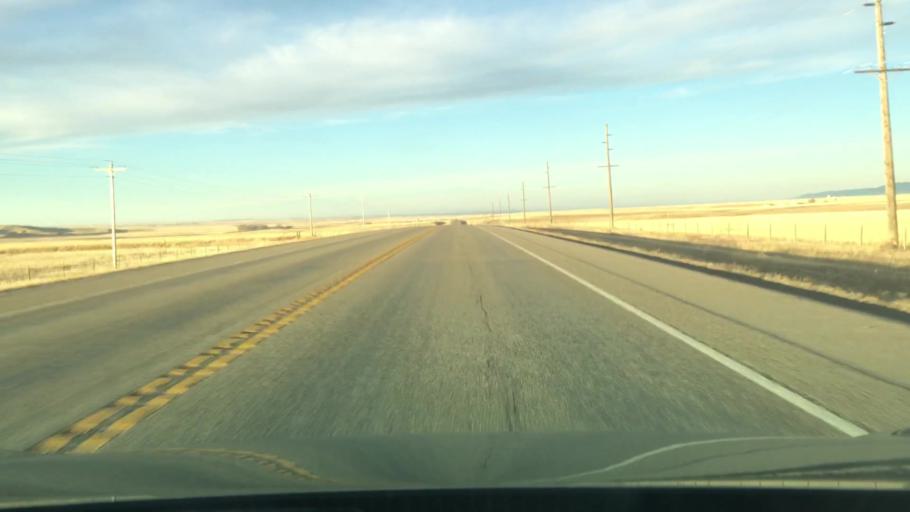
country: US
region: Montana
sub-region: Fergus County
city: Lewistown
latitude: 46.8623
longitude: -109.7647
